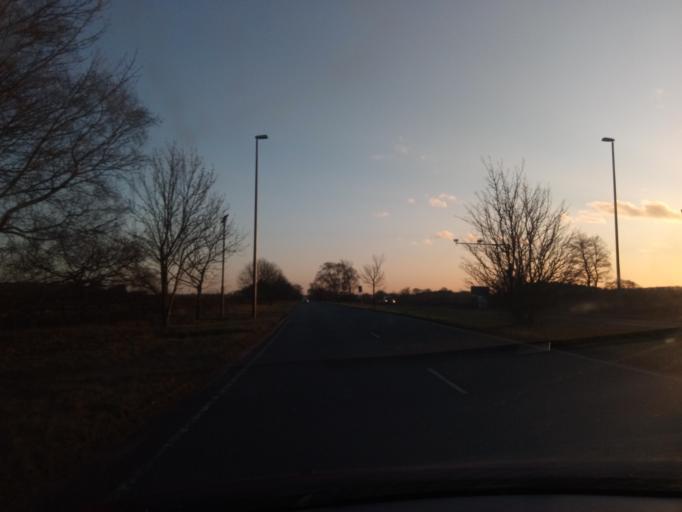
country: GB
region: England
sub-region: Nottinghamshire
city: Farnsfield
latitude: 53.0673
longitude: -1.0707
